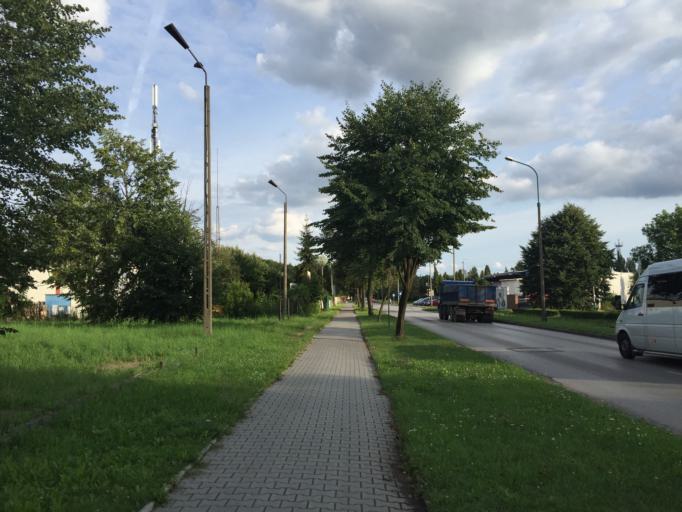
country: PL
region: Lesser Poland Voivodeship
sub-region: Powiat oswiecimski
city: Brzezinka
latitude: 50.0334
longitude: 19.1971
